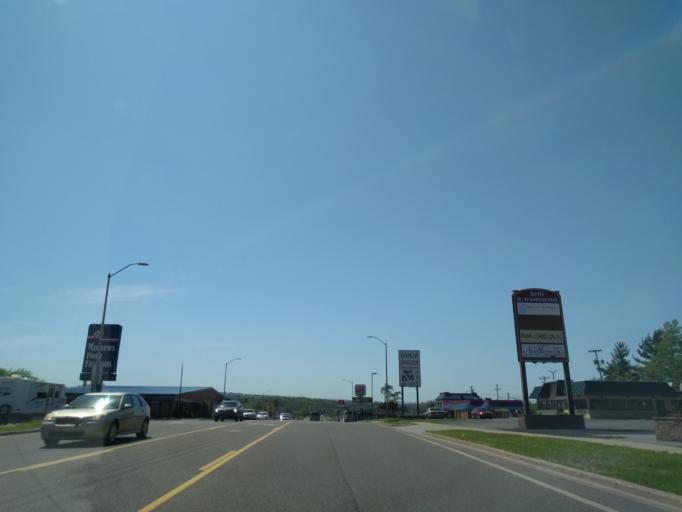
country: US
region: Michigan
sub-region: Marquette County
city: Marquette
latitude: 46.5459
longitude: -87.4161
